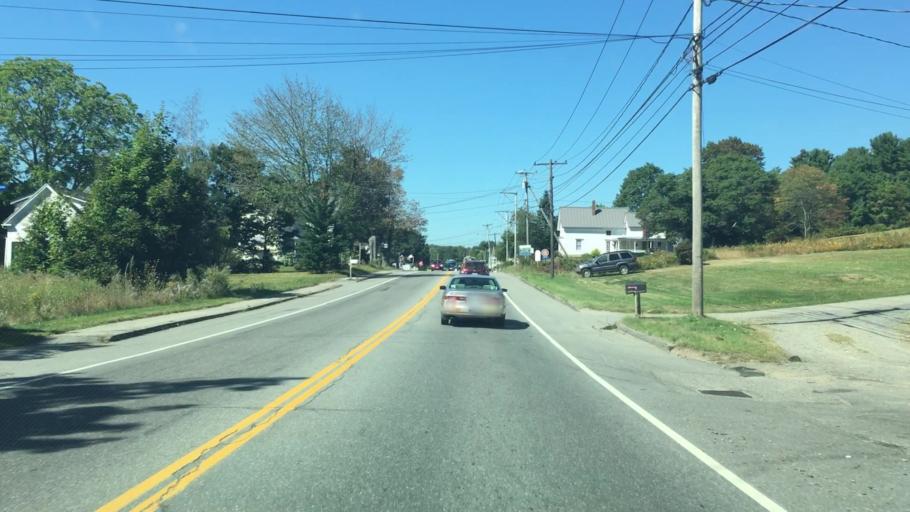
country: US
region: Maine
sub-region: Waldo County
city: Belfast
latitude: 44.4337
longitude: -68.9996
